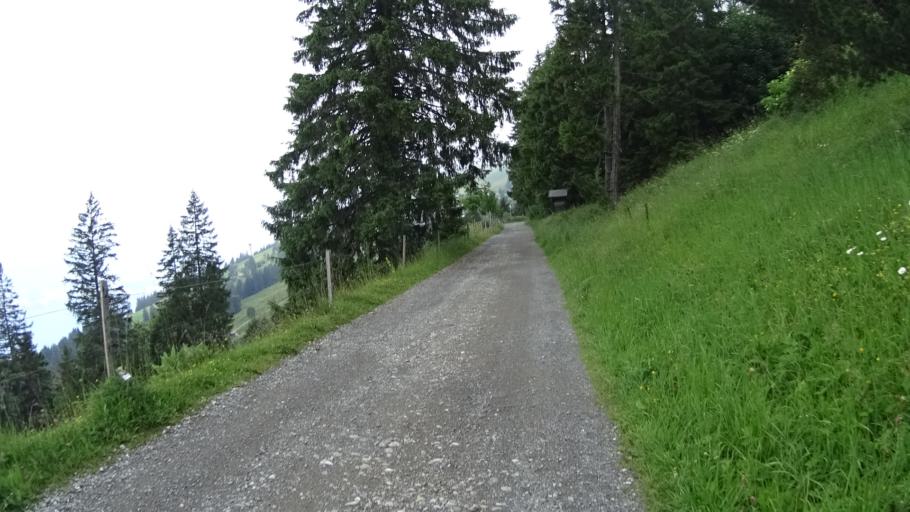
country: CH
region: Lucerne
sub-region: Lucerne-Land District
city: Vitznau
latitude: 47.0409
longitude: 8.4773
